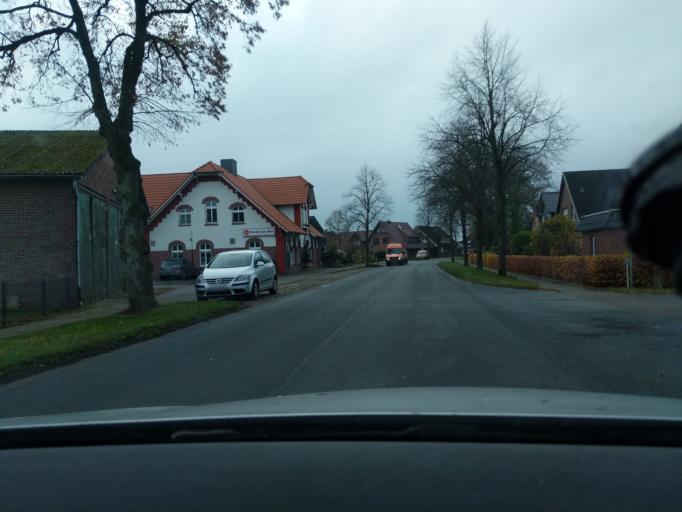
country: DE
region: Lower Saxony
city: Ahlerstedt
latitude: 53.3661
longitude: 9.4281
